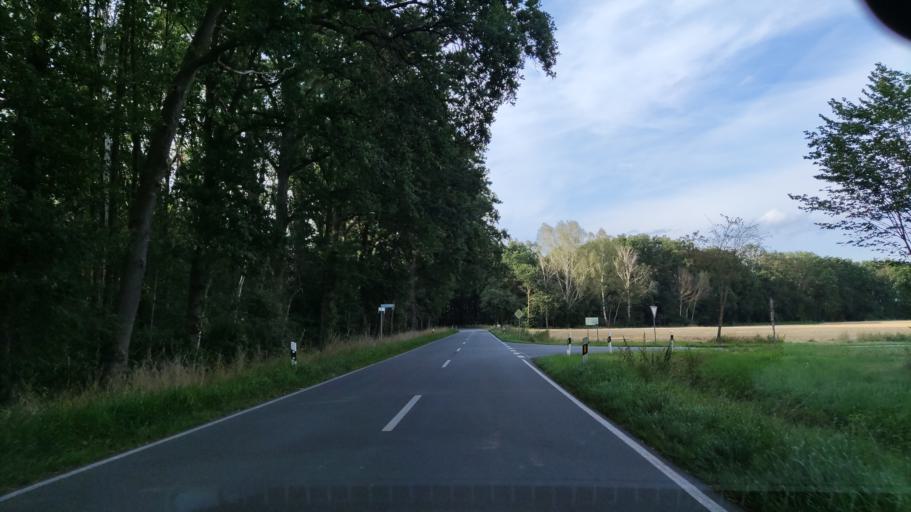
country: DE
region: Lower Saxony
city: Dannenberg
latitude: 53.1117
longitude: 11.1122
